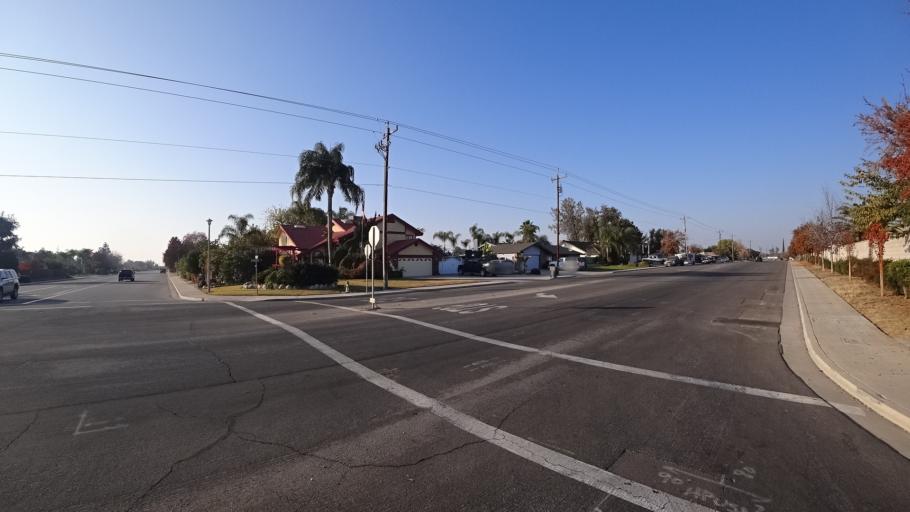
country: US
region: California
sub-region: Kern County
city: Rosedale
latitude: 35.3763
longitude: -119.1544
